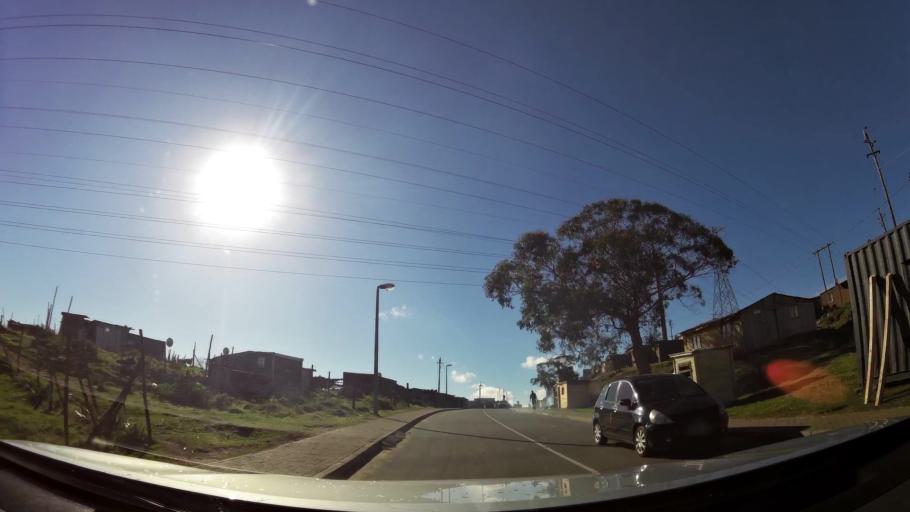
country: ZA
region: Western Cape
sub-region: Eden District Municipality
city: Knysna
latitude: -34.0281
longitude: 23.0635
